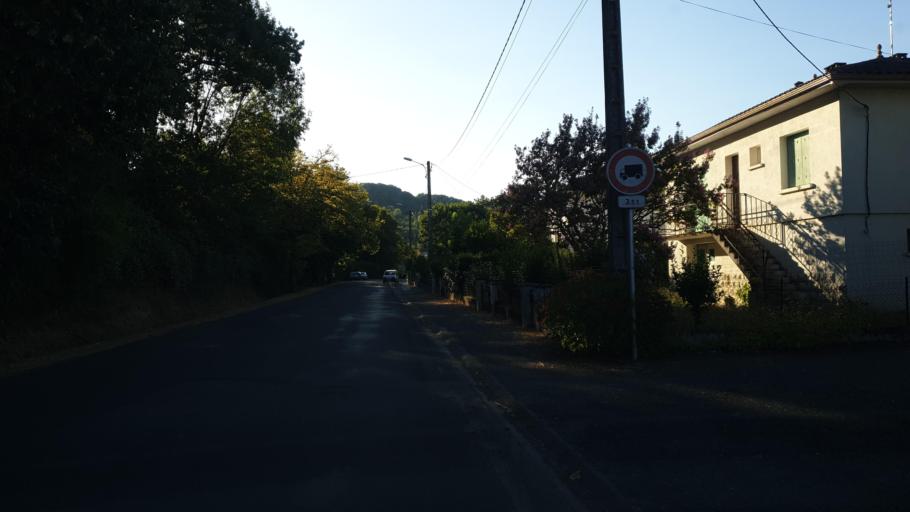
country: FR
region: Aquitaine
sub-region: Departement du Lot-et-Garonne
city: Castelmoron-sur-Lot
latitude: 44.3944
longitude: 0.4996
